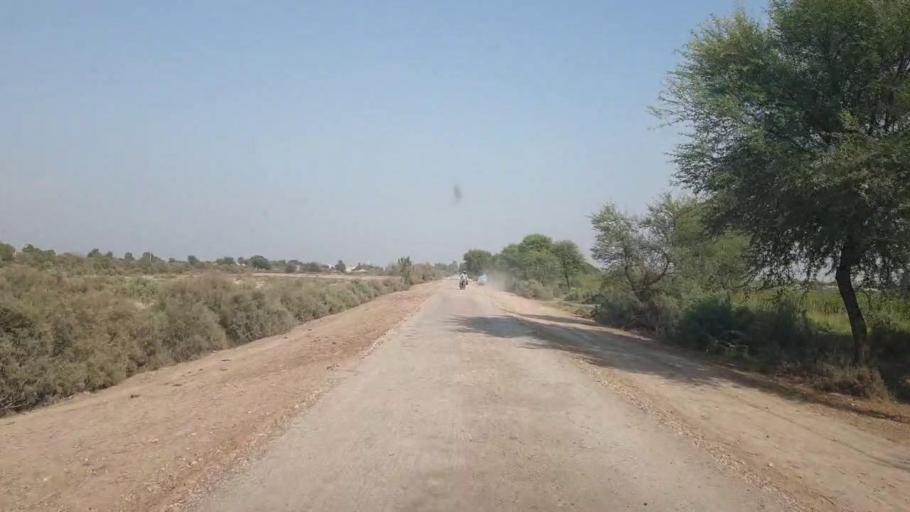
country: PK
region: Sindh
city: Sinjhoro
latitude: 26.0554
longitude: 68.8340
